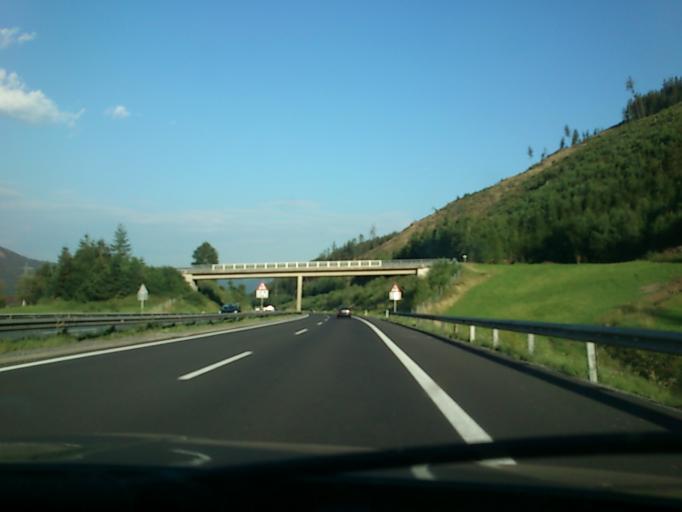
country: AT
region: Styria
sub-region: Politischer Bezirk Leoben
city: Kammern im Liesingtal
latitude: 47.3853
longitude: 14.9204
